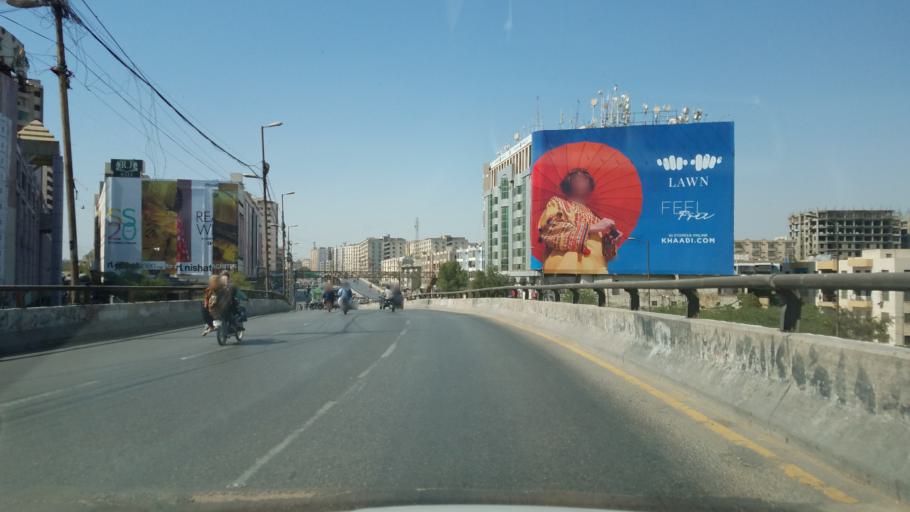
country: PK
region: Sindh
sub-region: Karachi District
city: Karachi
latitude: 24.9011
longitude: 67.1162
